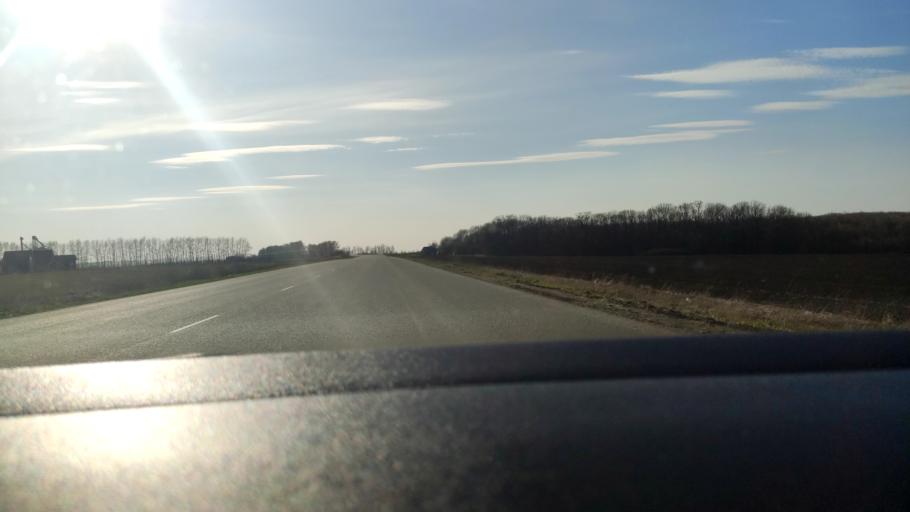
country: RU
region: Voronezj
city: Kolodeznyy
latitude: 51.3399
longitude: 39.0446
